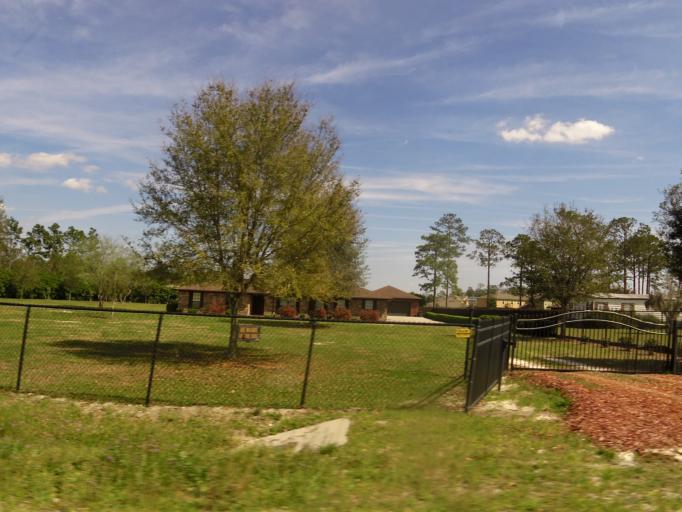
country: US
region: Florida
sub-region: Clay County
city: Middleburg
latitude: 30.1023
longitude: -81.8645
